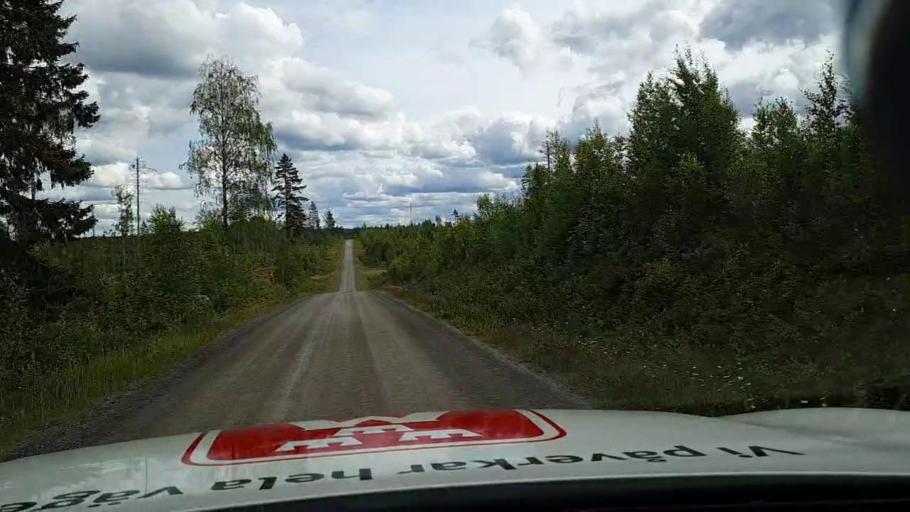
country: SE
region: Jaemtland
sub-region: OEstersunds Kommun
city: Lit
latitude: 63.2966
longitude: 15.3310
